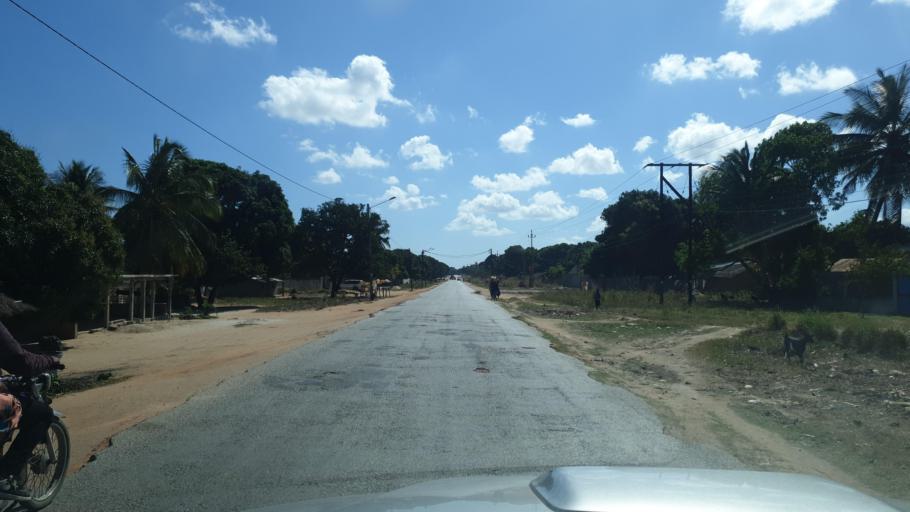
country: MZ
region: Nampula
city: Nacala
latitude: -14.5180
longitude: 40.6959
